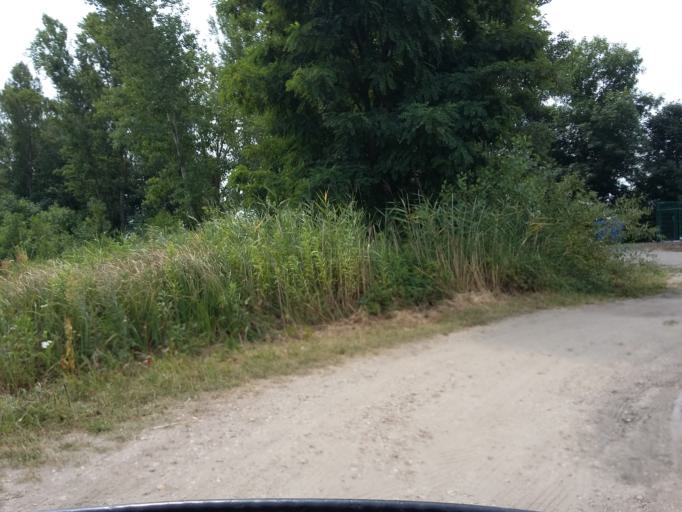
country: AT
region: Lower Austria
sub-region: Politischer Bezirk Ganserndorf
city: Drosing
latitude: 48.4955
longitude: 16.9468
